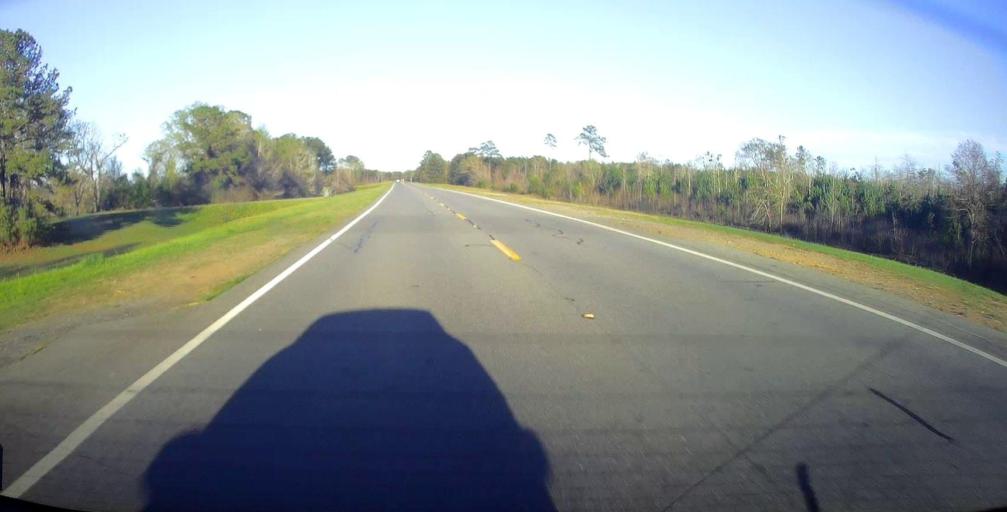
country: US
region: Georgia
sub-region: Wilcox County
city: Abbeville
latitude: 31.9987
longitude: -83.2666
